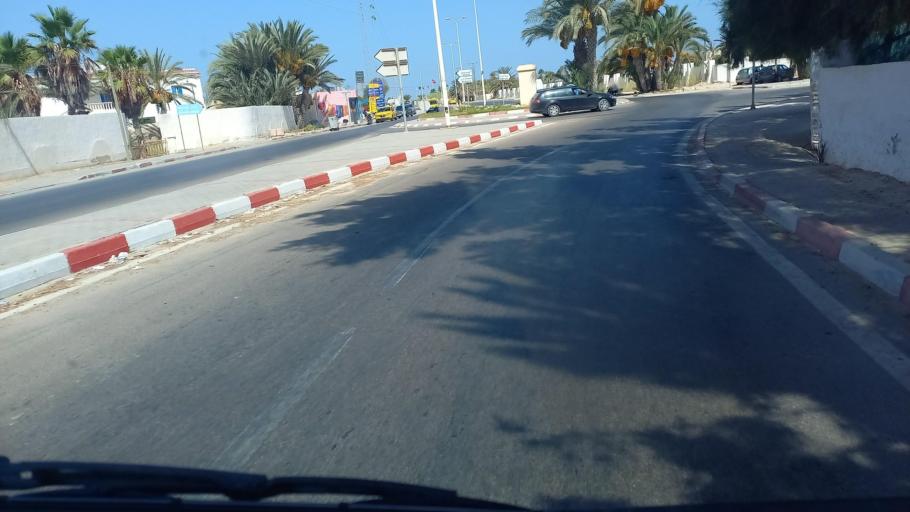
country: TN
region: Madanin
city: Midoun
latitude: 33.8669
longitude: 10.9600
